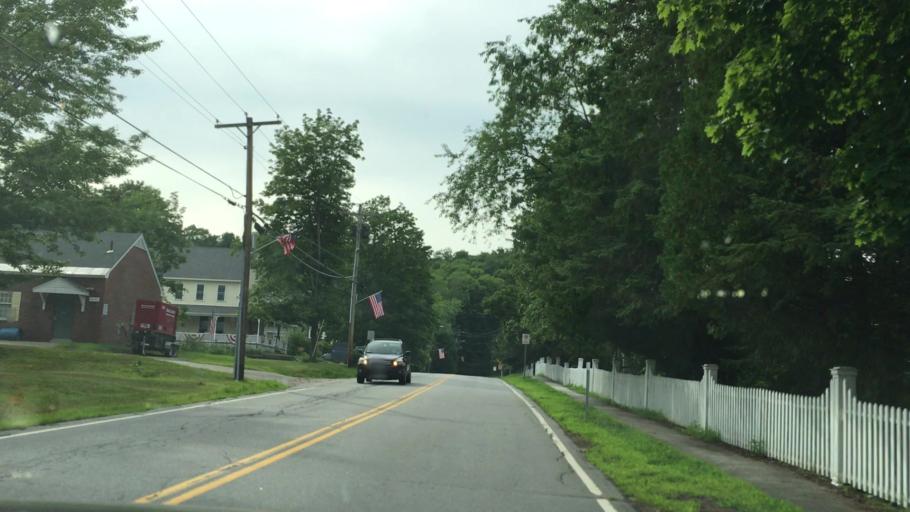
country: US
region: New Hampshire
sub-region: Carroll County
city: Center Harbor
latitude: 43.7094
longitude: -71.4640
